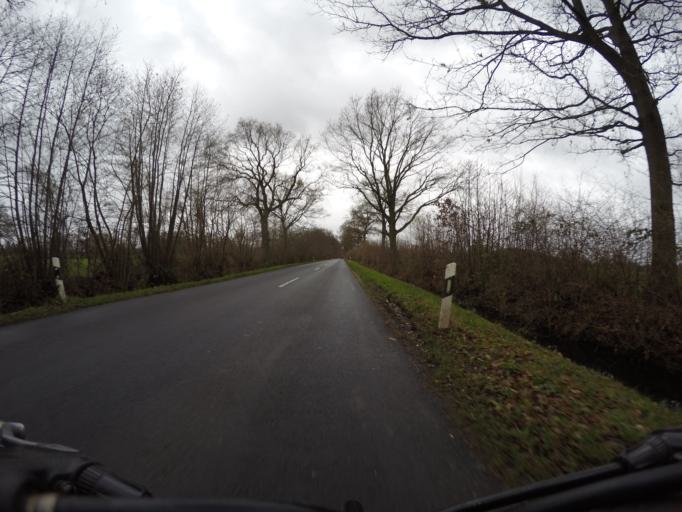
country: DE
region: Schleswig-Holstein
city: Hasloh
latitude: 53.7068
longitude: 9.8795
